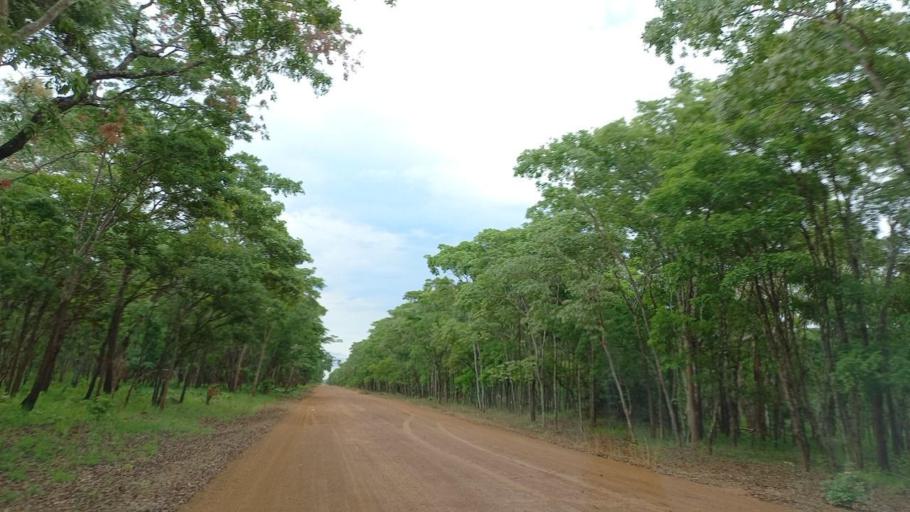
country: ZM
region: North-Western
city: Kalengwa
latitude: -13.3614
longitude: 25.0758
